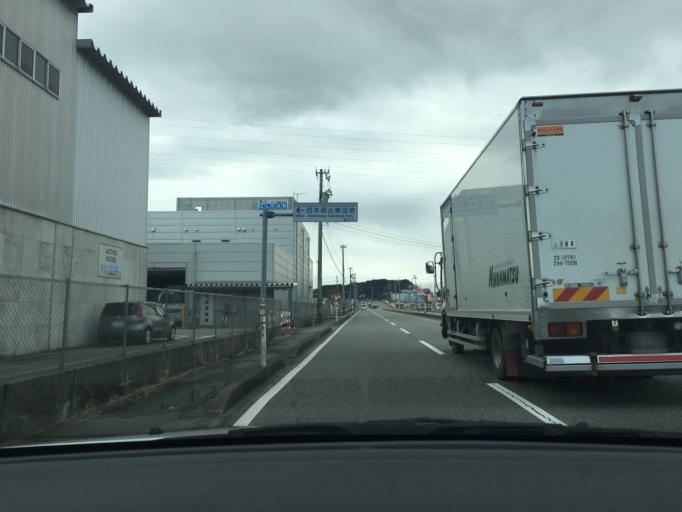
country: JP
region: Toyama
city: Toyama-shi
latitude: 36.6822
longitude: 137.1691
